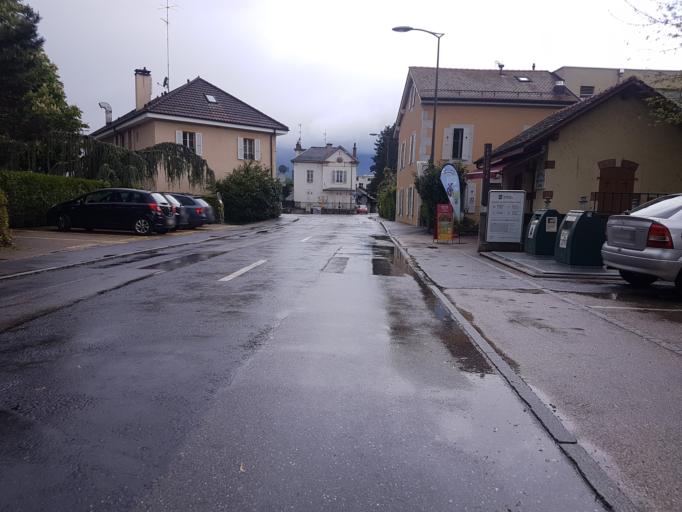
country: CH
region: Geneva
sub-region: Geneva
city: Dardagny
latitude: 46.1779
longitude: 6.0018
